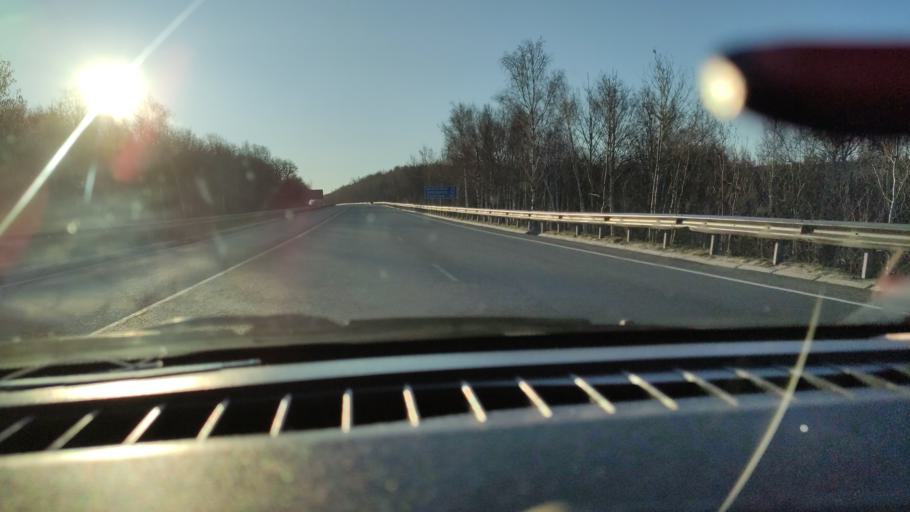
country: RU
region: Saratov
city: Vol'sk
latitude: 52.1129
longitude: 47.3178
